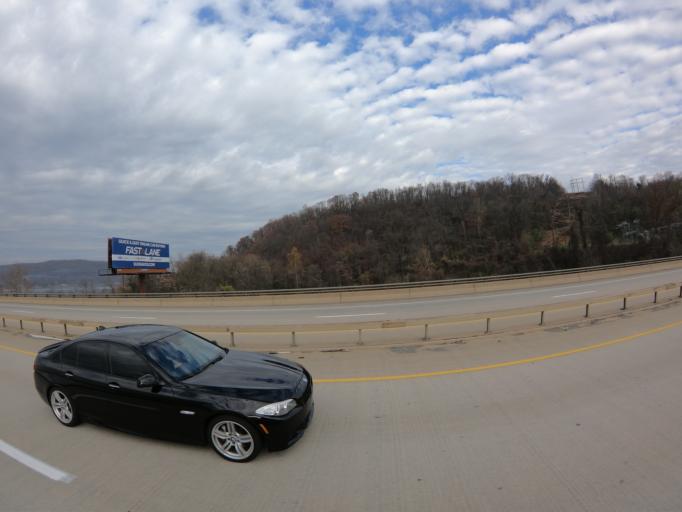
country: US
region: Pennsylvania
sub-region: Lancaster County
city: Columbia
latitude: 40.0374
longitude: -76.5138
